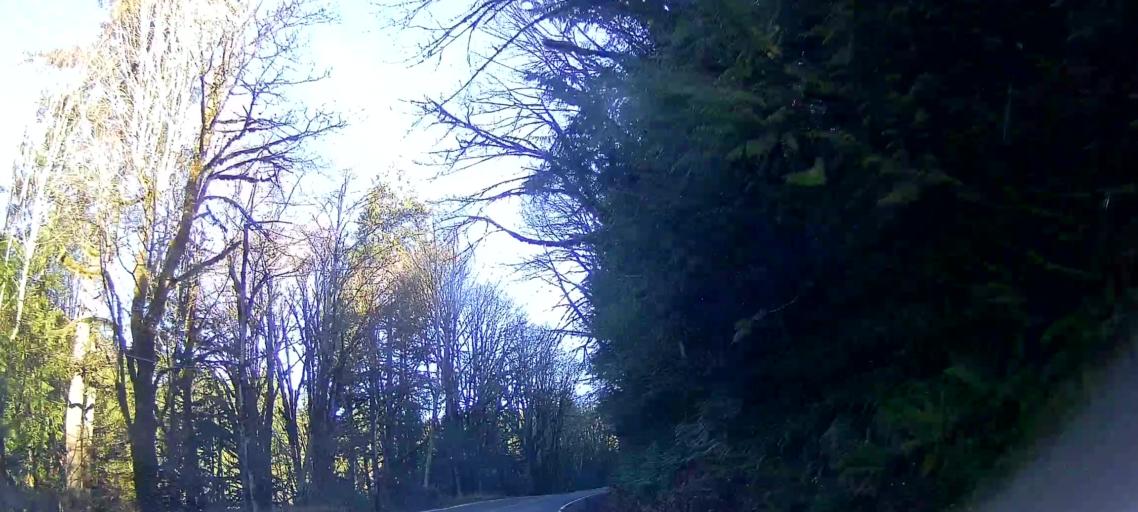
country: US
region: Washington
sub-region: Snohomish County
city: Darrington
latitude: 48.5465
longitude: -121.7700
